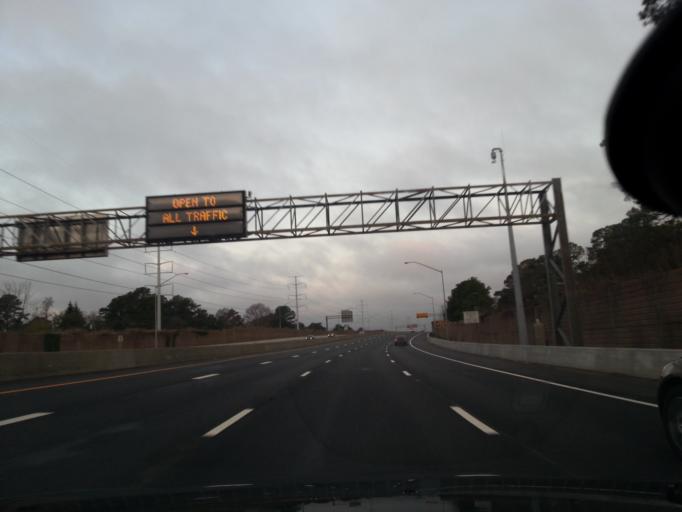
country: US
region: Virginia
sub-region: City of Chesapeake
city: Chesapeake
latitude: 36.8422
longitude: -76.2297
